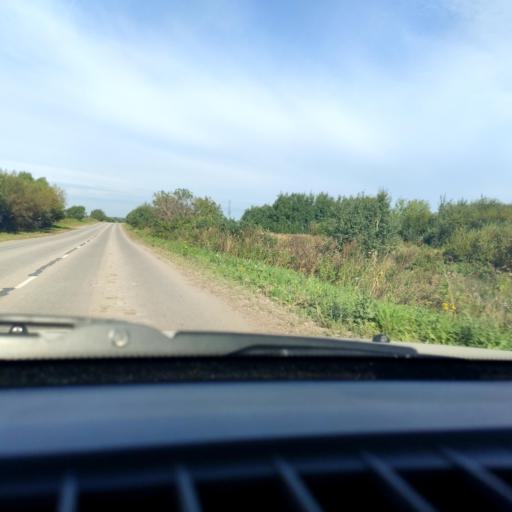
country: RU
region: Perm
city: Kondratovo
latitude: 57.9996
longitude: 56.0743
